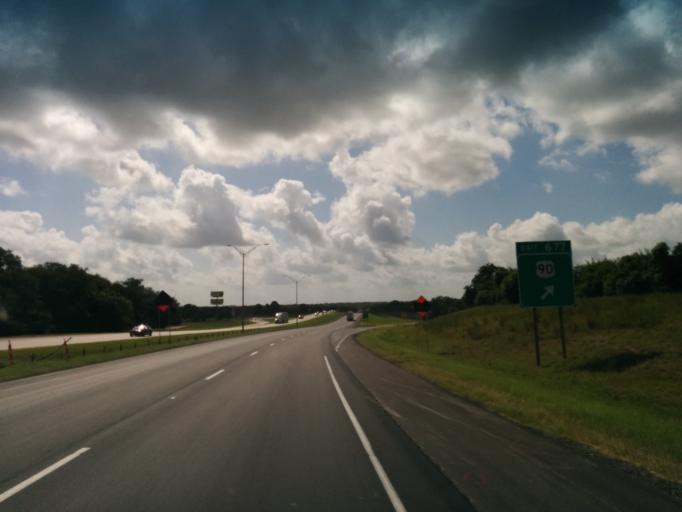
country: US
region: Texas
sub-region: Fayette County
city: Schulenburg
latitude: 29.6959
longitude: -96.8538
